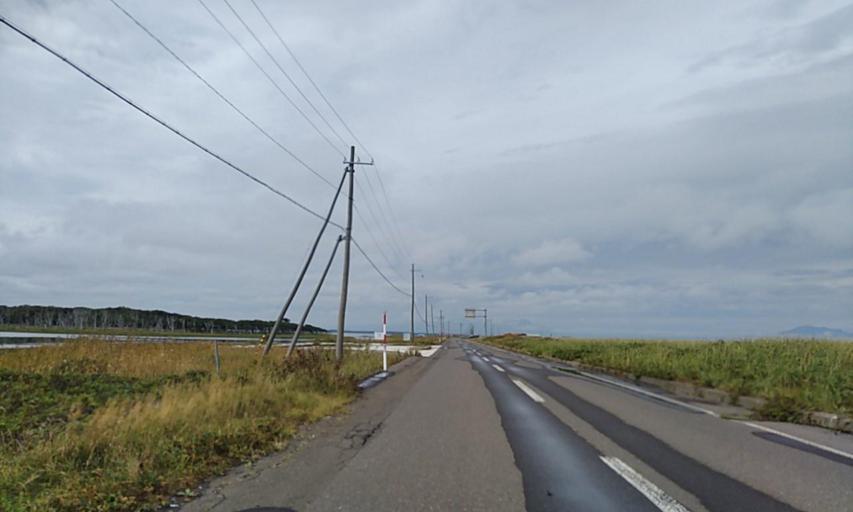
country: JP
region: Hokkaido
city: Shibetsu
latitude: 43.6089
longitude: 145.2756
